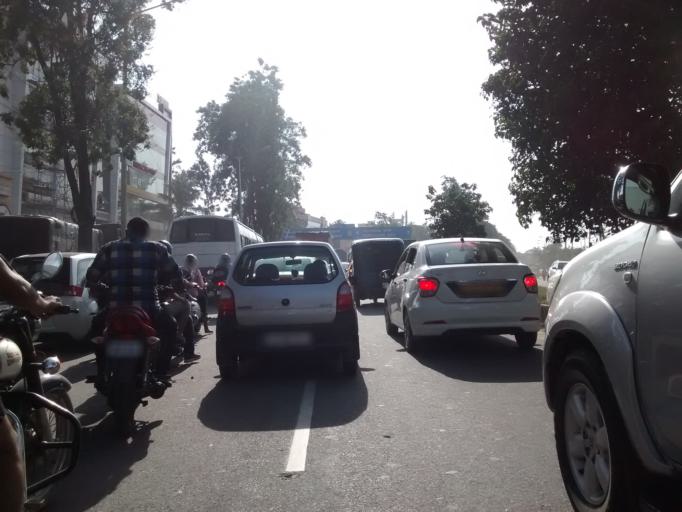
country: IN
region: Karnataka
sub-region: Bangalore Urban
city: Yelahanka
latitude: 13.0419
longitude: 77.5948
